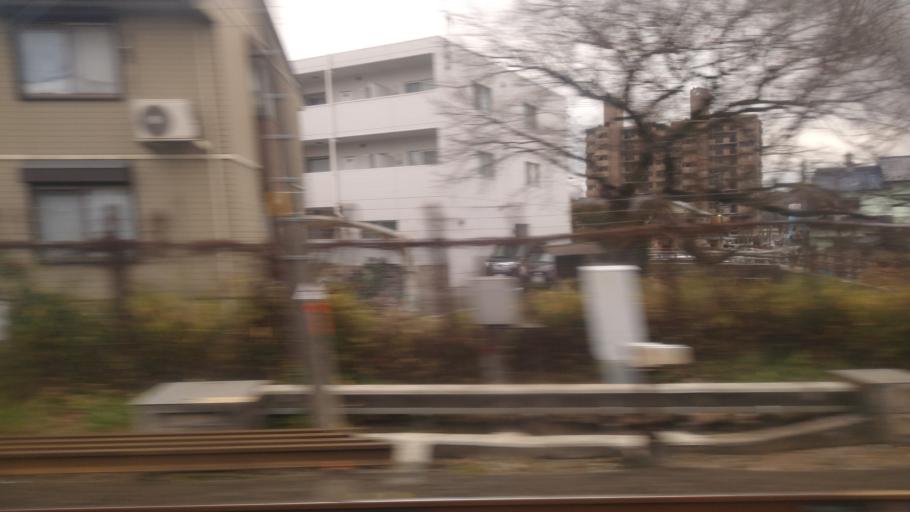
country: JP
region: Gifu
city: Toki
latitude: 35.3616
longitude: 137.1852
